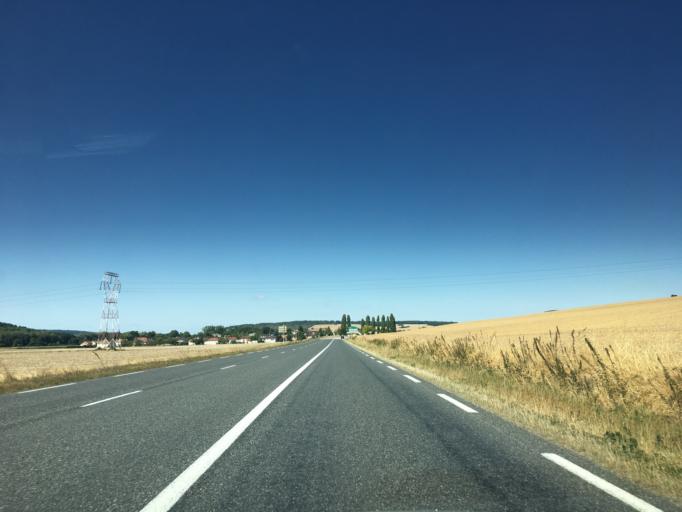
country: FR
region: Bourgogne
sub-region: Departement de l'Yonne
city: Villeneuve-sur-Yonne
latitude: 48.0673
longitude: 3.2912
